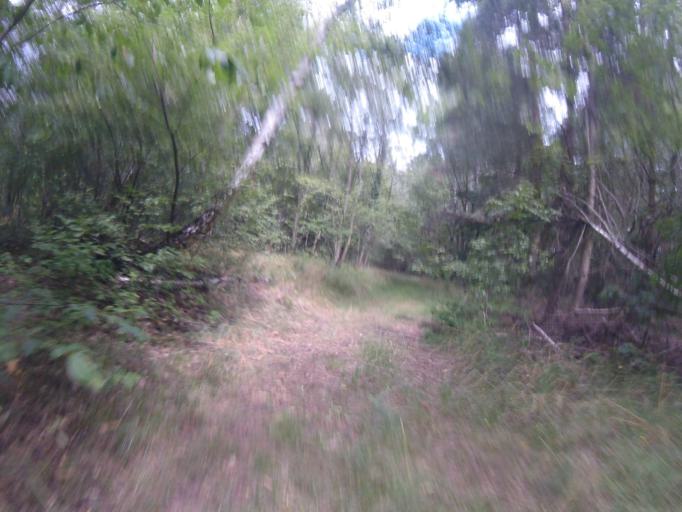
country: DE
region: Brandenburg
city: Konigs Wusterhausen
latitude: 52.3062
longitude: 13.6204
